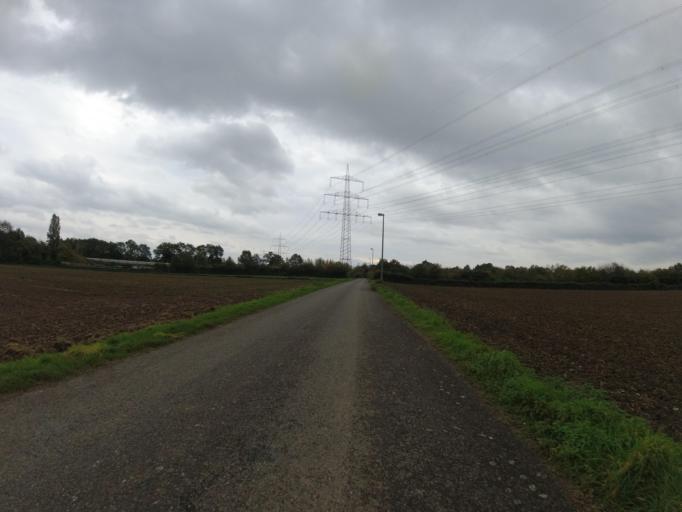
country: DE
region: North Rhine-Westphalia
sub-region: Regierungsbezirk Dusseldorf
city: Hochfeld
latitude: 51.3891
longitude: 6.6903
